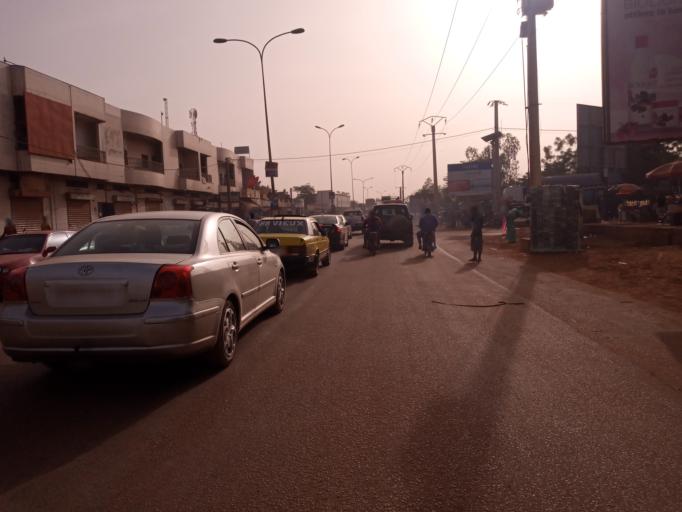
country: ML
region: Bamako
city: Bamako
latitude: 12.6673
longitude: -7.9289
